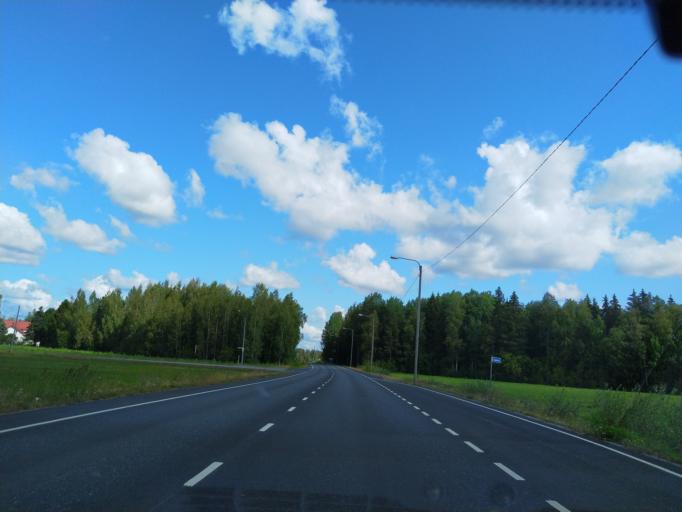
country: FI
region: Satakunta
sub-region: Pori
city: Huittinen
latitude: 61.1746
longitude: 22.7104
